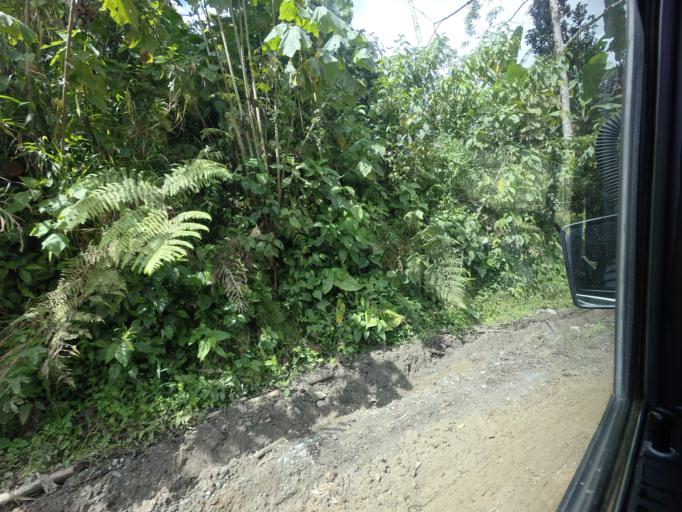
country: CO
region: Huila
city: Isnos
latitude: 1.9570
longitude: -76.2848
